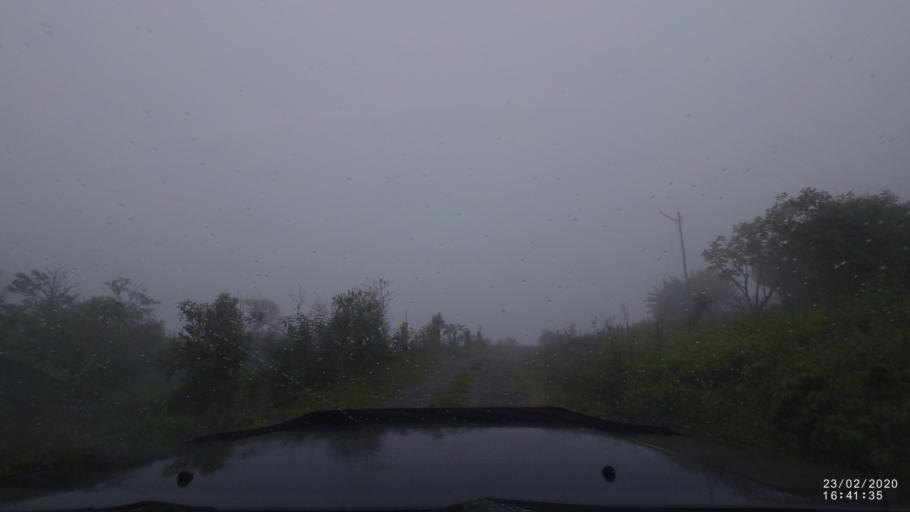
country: BO
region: Cochabamba
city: Colomi
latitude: -17.0822
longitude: -66.0027
